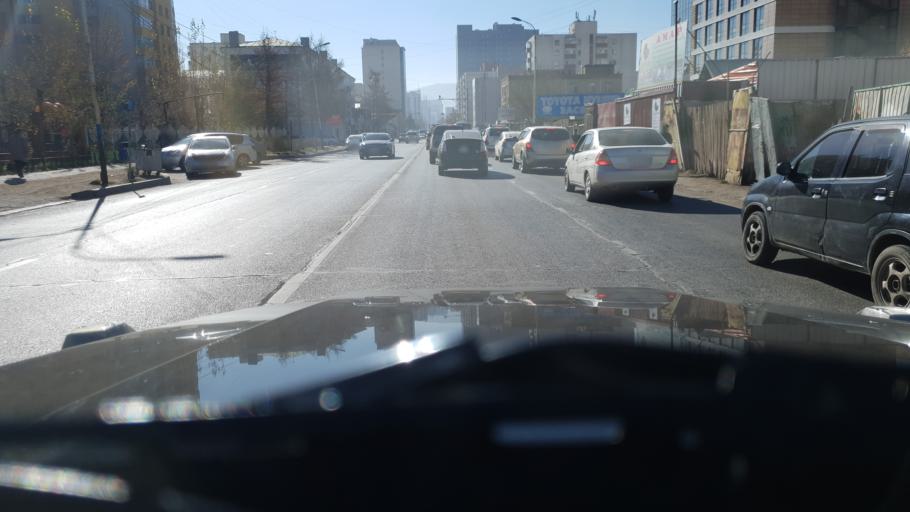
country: MN
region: Ulaanbaatar
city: Ulaanbaatar
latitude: 47.9308
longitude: 106.9168
